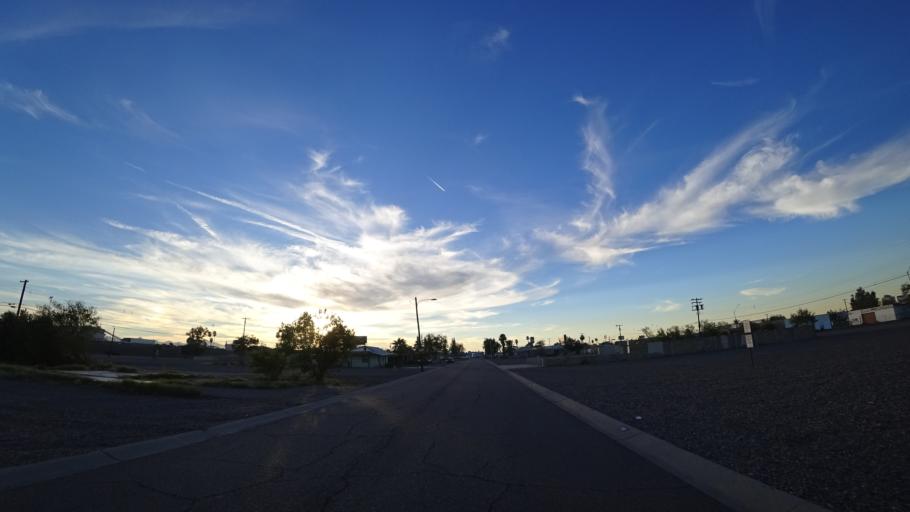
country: US
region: Arizona
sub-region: Maricopa County
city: Phoenix
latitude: 33.4304
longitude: -112.0621
